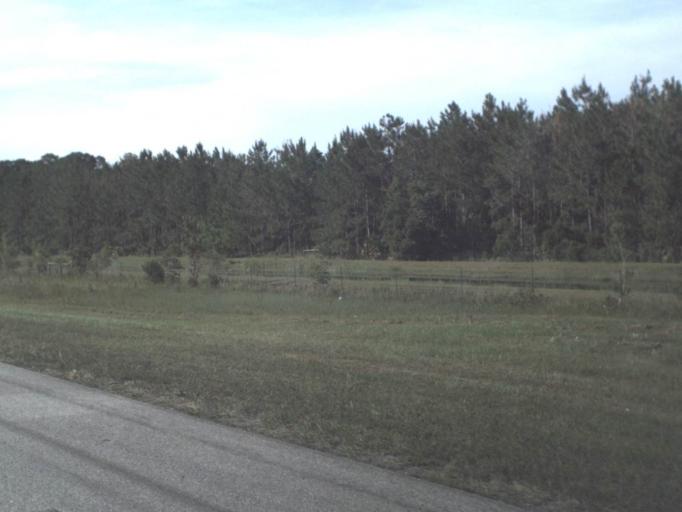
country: US
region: Florida
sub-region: Saint Johns County
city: Saint Augustine Shores
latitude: 29.8045
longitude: -81.3691
